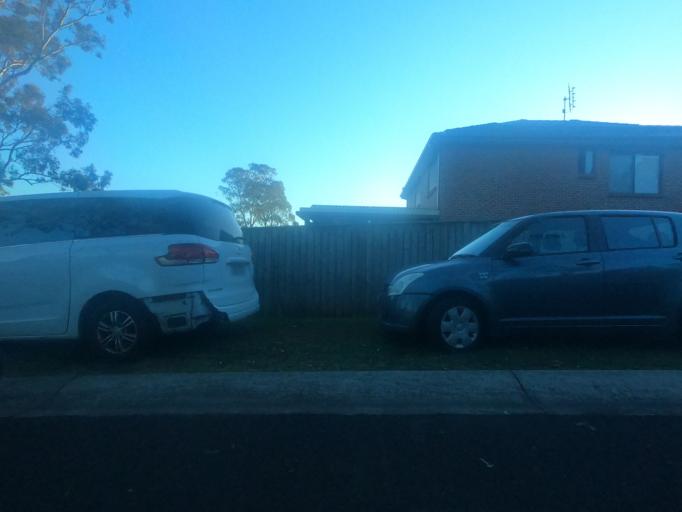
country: AU
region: New South Wales
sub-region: Wollongong
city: Dapto
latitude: -34.4926
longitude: 150.7645
